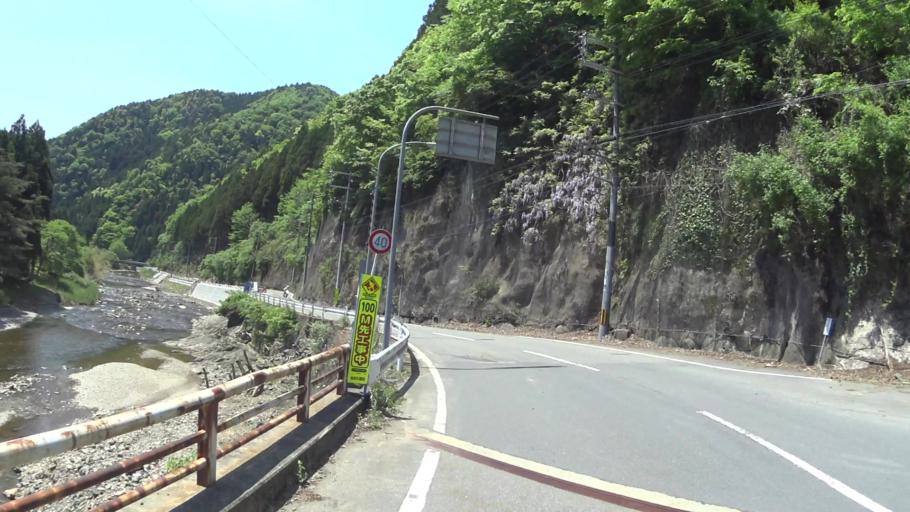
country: JP
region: Shiga Prefecture
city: Kitahama
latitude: 35.2077
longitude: 135.7498
